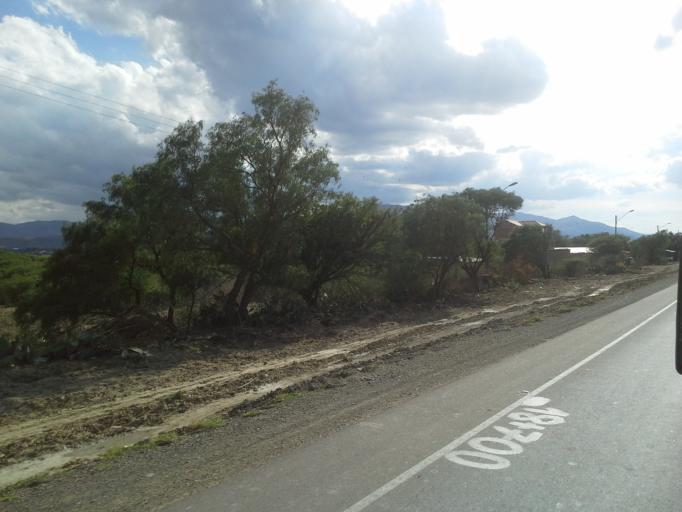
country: BO
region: Cochabamba
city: Tarata
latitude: -17.5448
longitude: -66.0090
